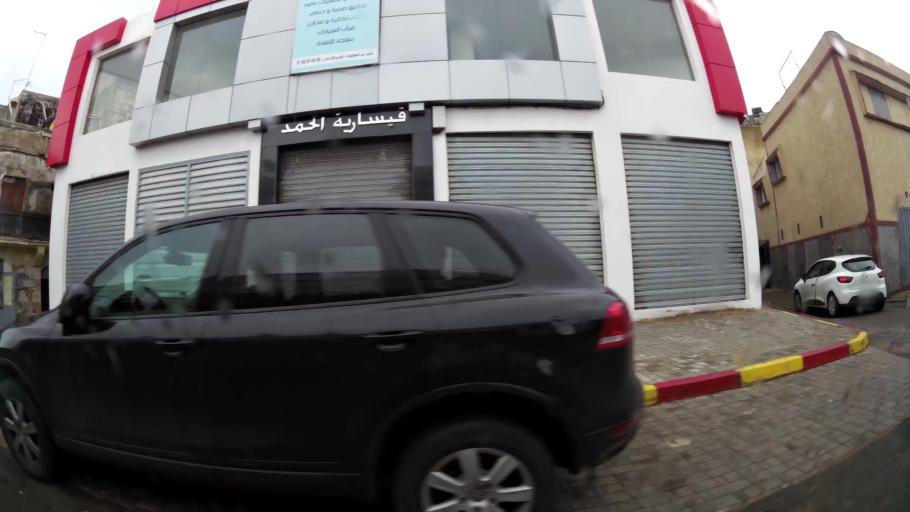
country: MA
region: Grand Casablanca
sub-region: Casablanca
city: Casablanca
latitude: 33.5784
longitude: -7.6015
